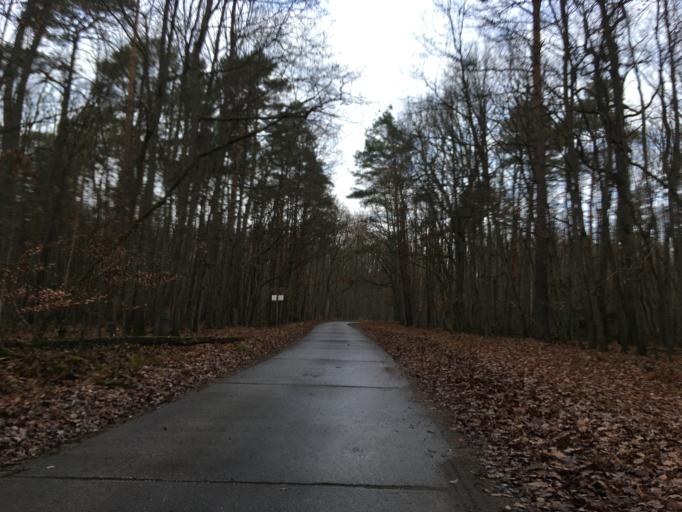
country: DE
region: Brandenburg
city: Tauer
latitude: 51.9480
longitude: 14.5167
